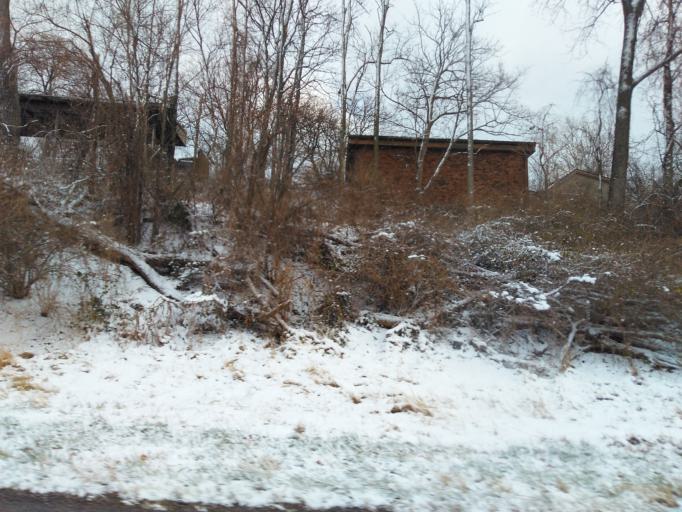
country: US
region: Illinois
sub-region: Madison County
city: Collinsville
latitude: 38.6922
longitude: -89.9993
